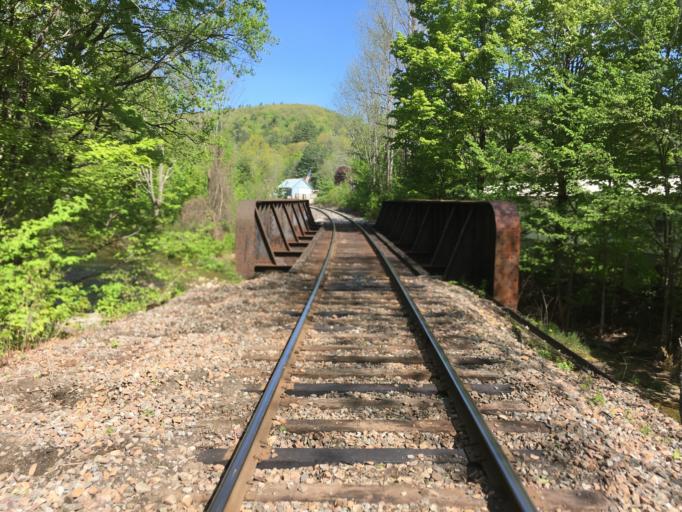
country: US
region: Vermont
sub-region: Windsor County
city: Chester
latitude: 43.3249
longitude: -72.6091
